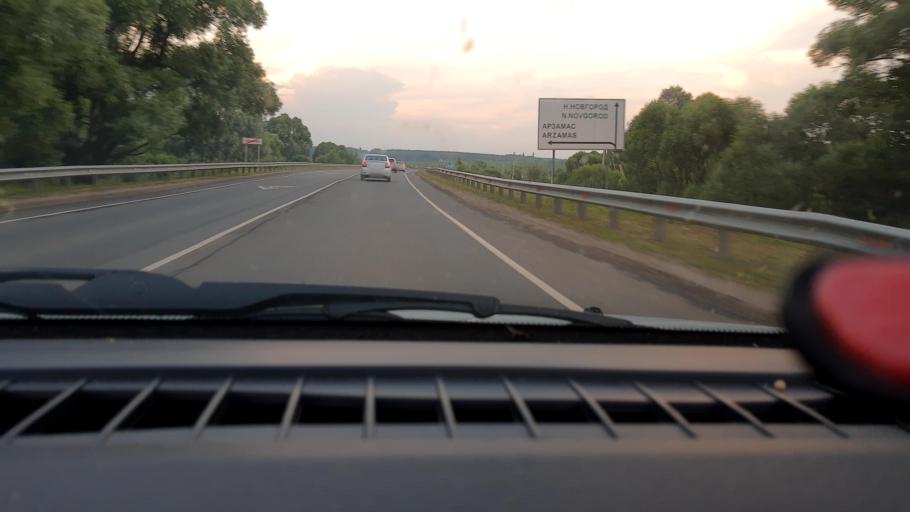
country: RU
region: Nizjnij Novgorod
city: Arzamas
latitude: 55.3306
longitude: 43.8884
